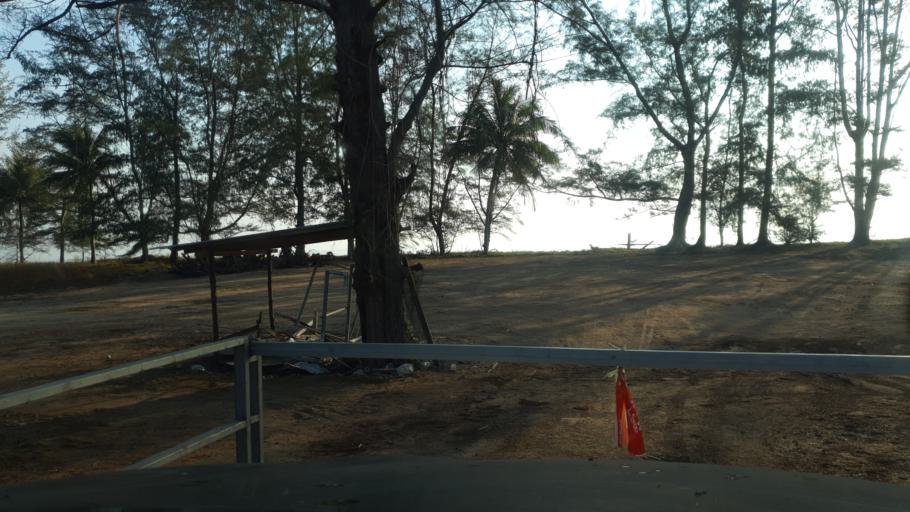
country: TH
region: Prachuap Khiri Khan
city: Bang Saphan
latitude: 11.3003
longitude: 99.5506
